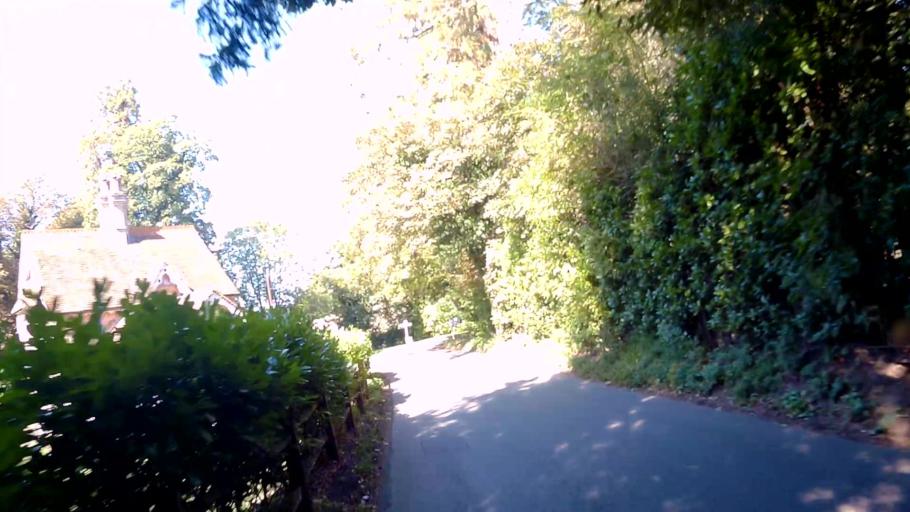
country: GB
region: England
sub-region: Hampshire
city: Overton
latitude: 51.2519
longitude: -1.1941
